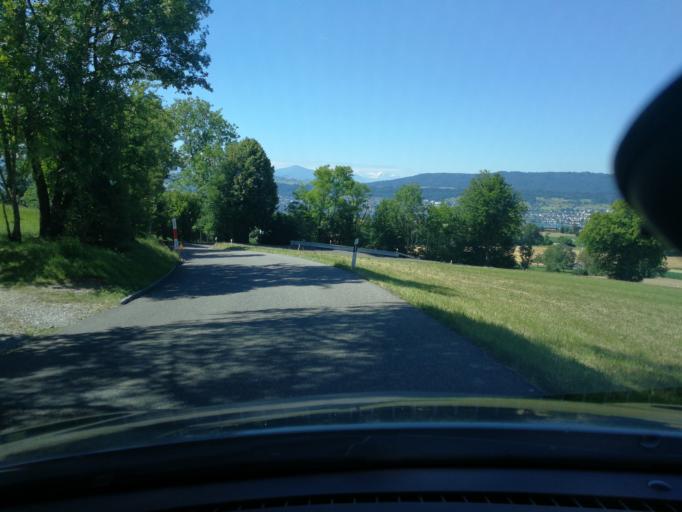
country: CH
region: Zurich
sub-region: Bezirk Meilen
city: Herrliberg
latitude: 47.2998
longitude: 8.6271
